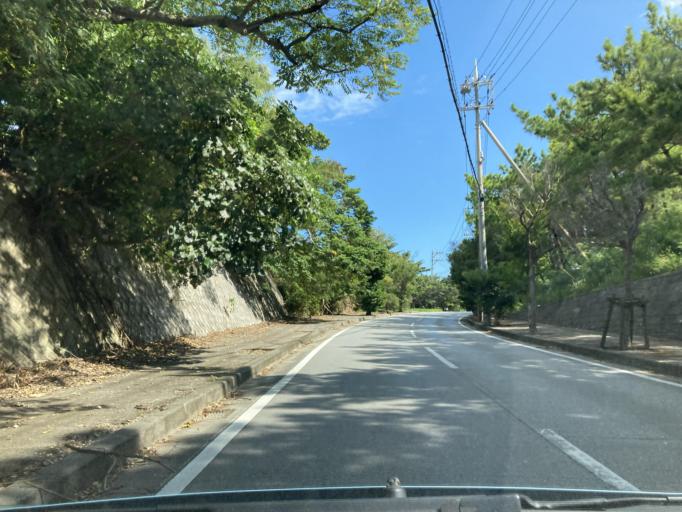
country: JP
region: Okinawa
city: Ginowan
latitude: 26.2435
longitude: 127.7571
